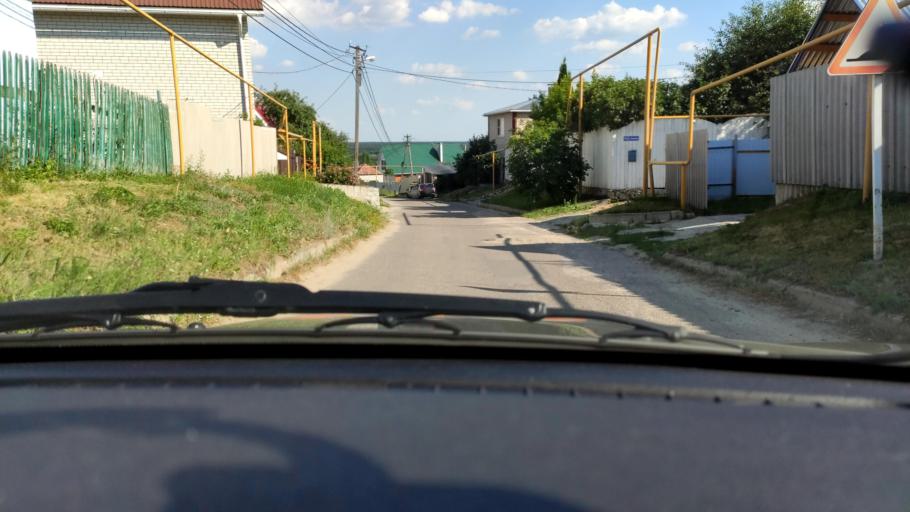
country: RU
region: Voronezj
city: Ramon'
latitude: 51.8221
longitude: 39.2753
